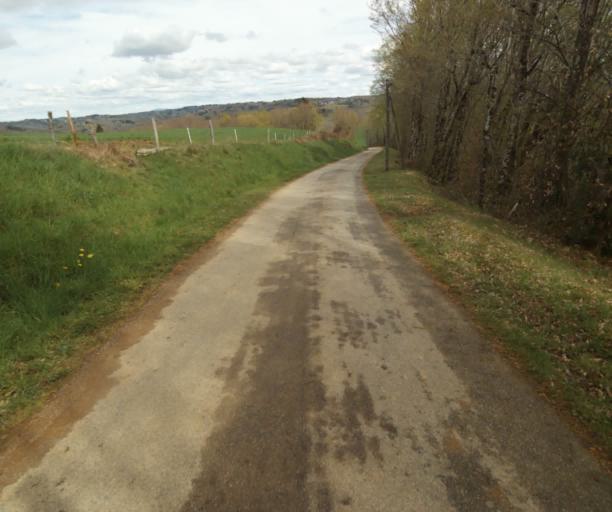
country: FR
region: Limousin
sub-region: Departement de la Correze
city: Laguenne
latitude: 45.2280
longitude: 1.8489
